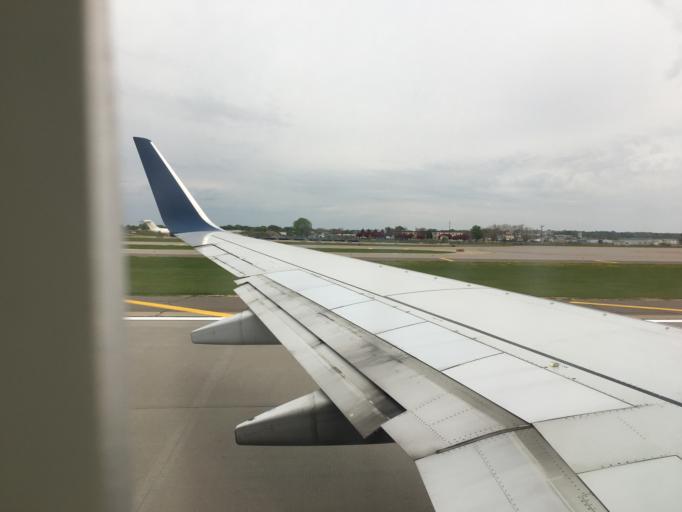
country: US
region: Minnesota
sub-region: Hennepin County
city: Richfield
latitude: 44.8864
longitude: -93.2308
